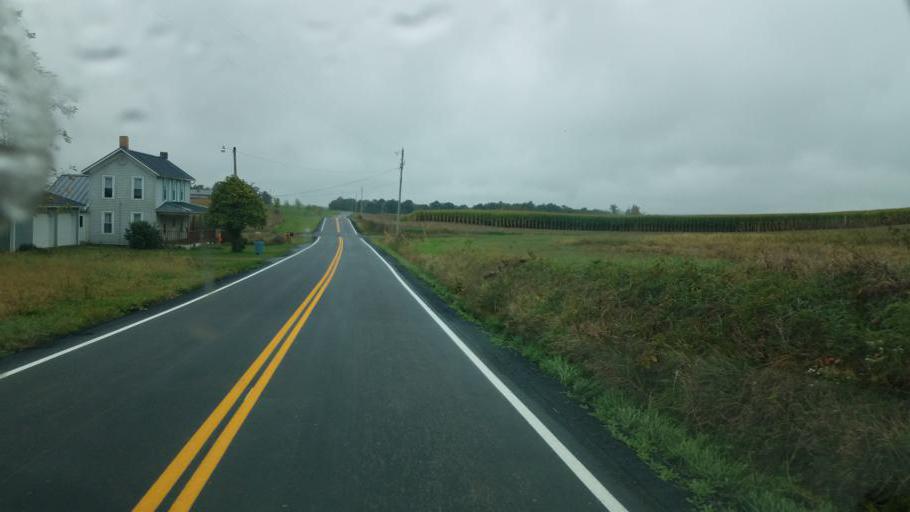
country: US
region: Ohio
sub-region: Wayne County
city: Shreve
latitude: 40.6180
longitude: -82.0601
